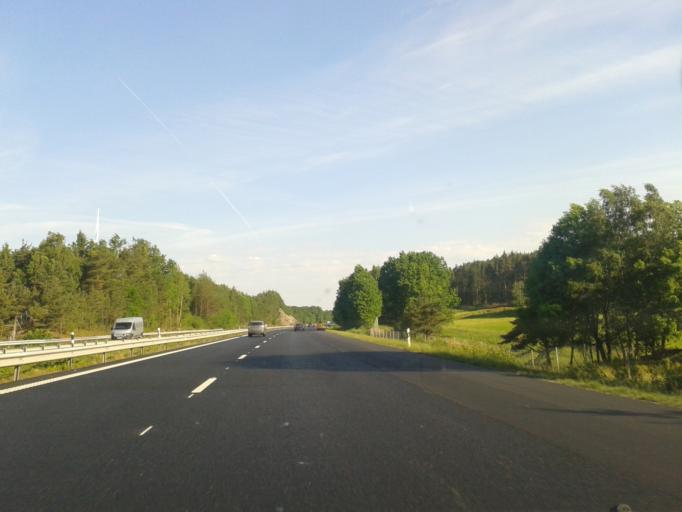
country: SE
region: Vaestra Goetaland
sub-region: Kungalvs Kommun
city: Kode
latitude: 57.9187
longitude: 11.8833
